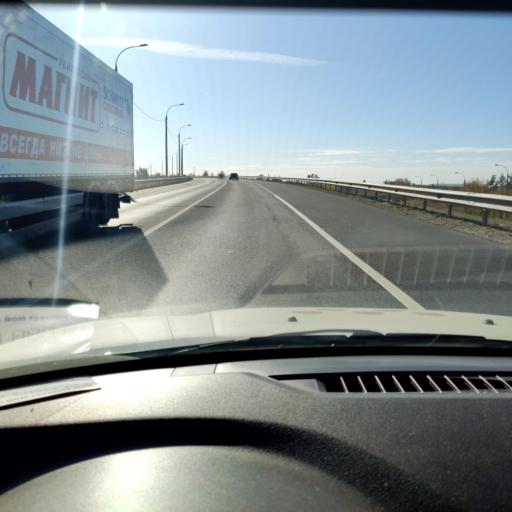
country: RU
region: Samara
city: Zhigulevsk
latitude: 53.5026
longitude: 49.5388
